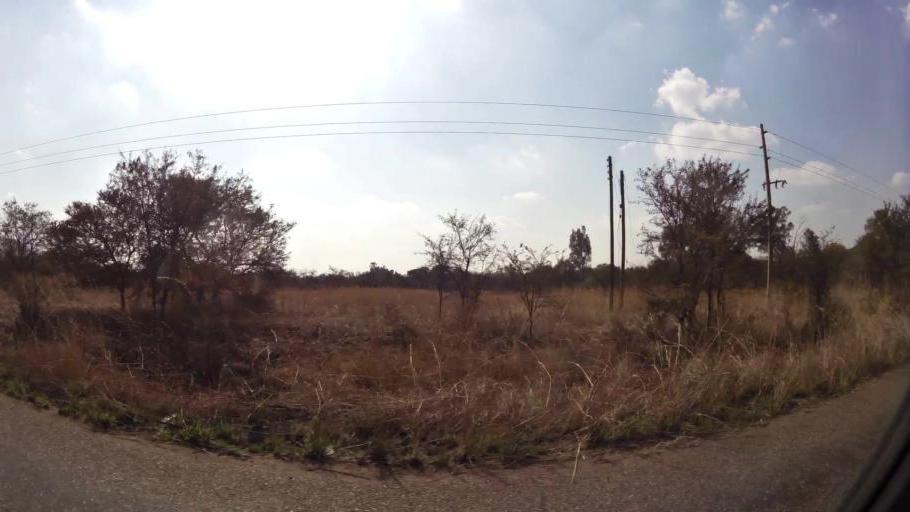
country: ZA
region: North-West
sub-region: Bojanala Platinum District Municipality
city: Rustenburg
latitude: -25.6344
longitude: 27.1622
